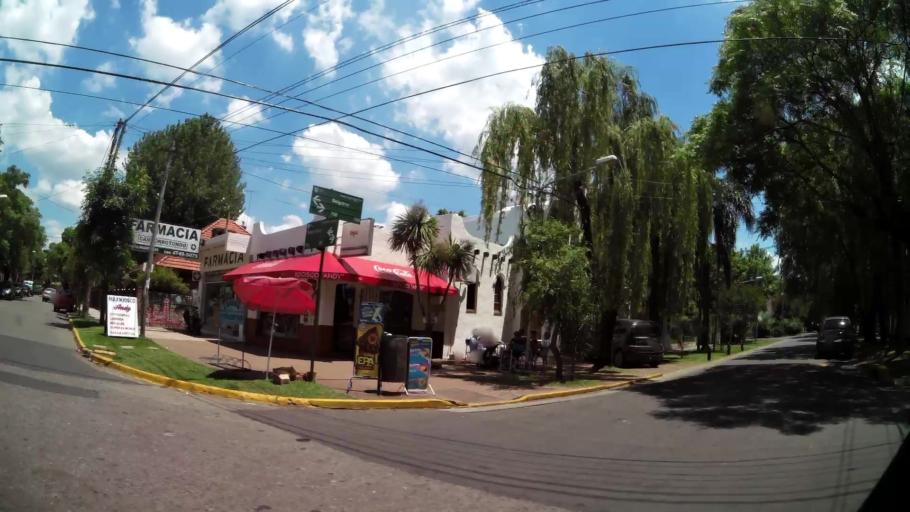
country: AR
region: Buenos Aires
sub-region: Partido de Tigre
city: Tigre
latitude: -34.4172
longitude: -58.5876
